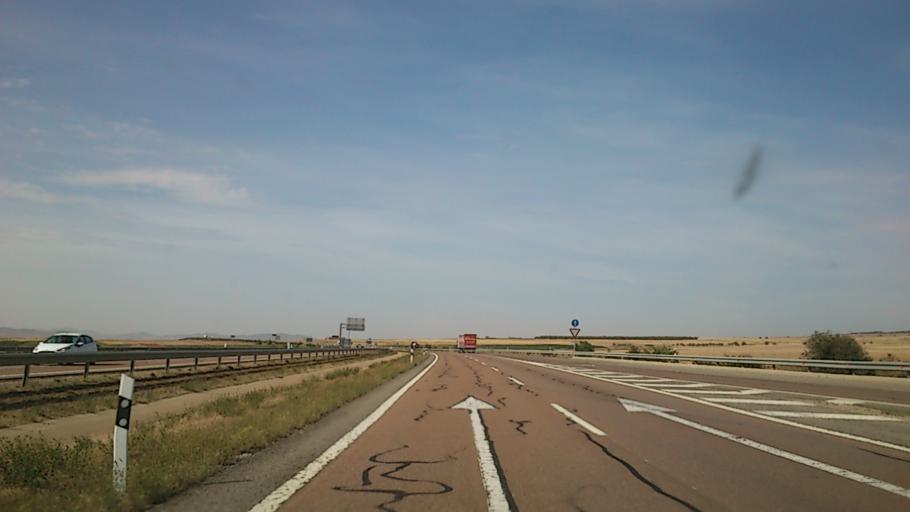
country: ES
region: Aragon
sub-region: Provincia de Teruel
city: Villafranca del Campo
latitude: 40.7038
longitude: -1.3204
